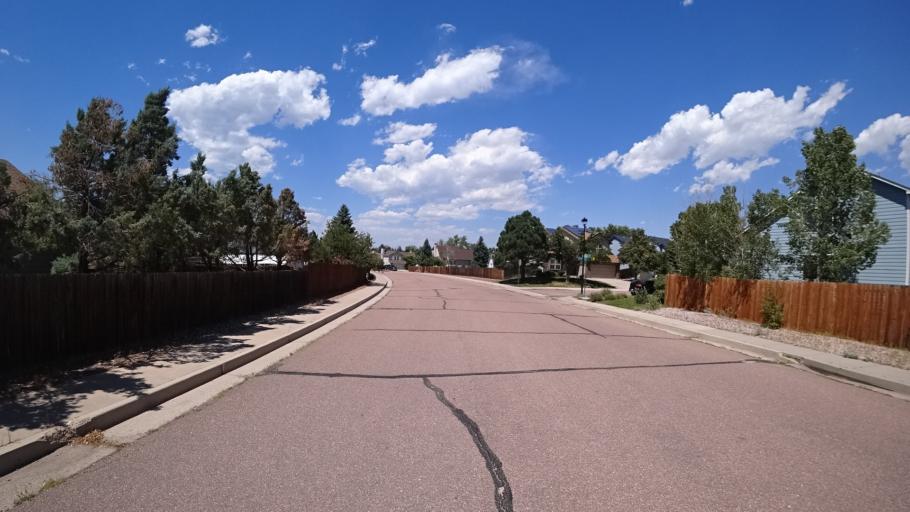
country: US
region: Colorado
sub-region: El Paso County
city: Black Forest
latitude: 38.9531
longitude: -104.7454
